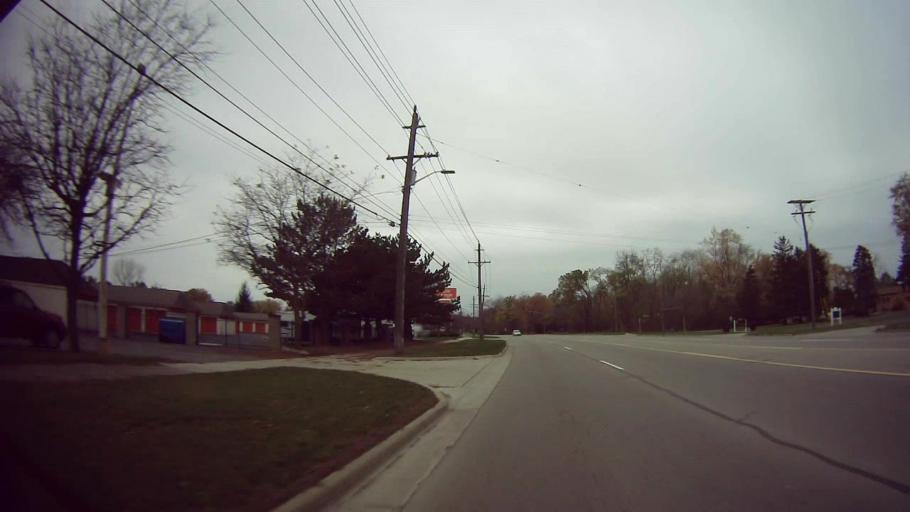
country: US
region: Michigan
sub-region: Oakland County
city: Pontiac
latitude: 42.6745
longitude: -83.3422
